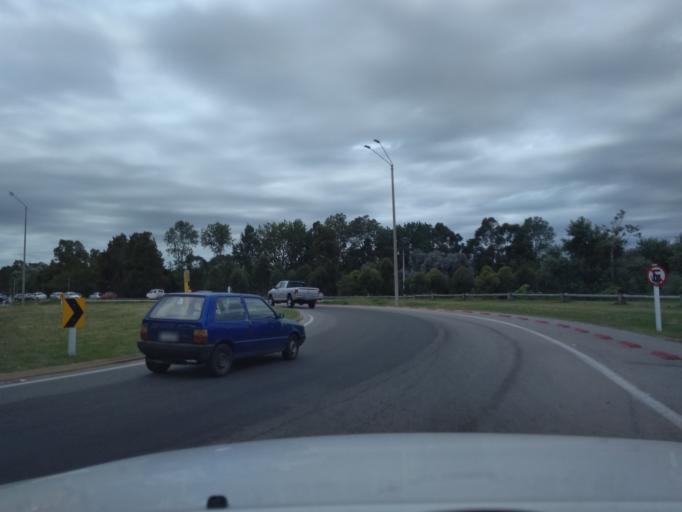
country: UY
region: Canelones
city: Barra de Carrasco
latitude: -34.8410
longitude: -56.0129
